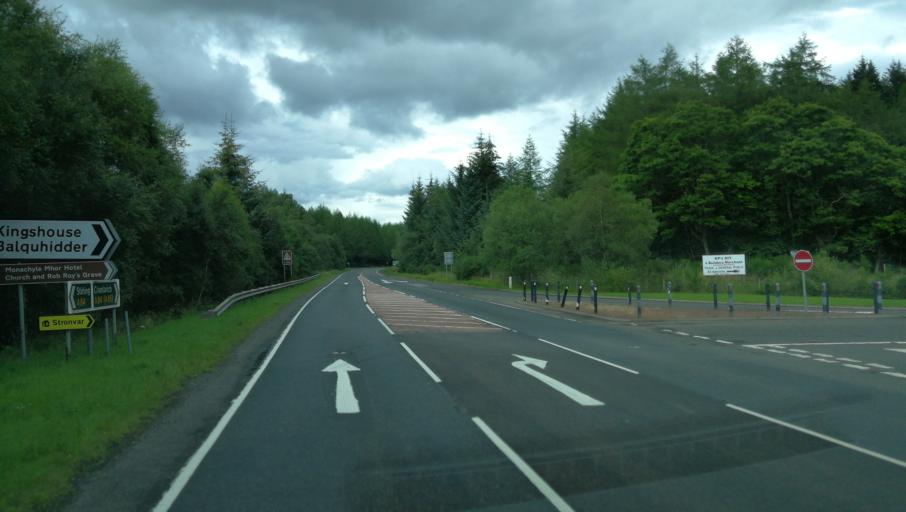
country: GB
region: Scotland
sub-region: Stirling
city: Callander
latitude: 56.3544
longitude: -4.3253
